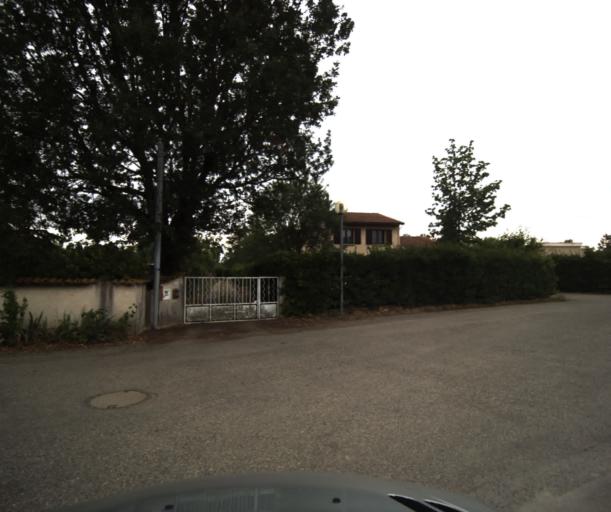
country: FR
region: Midi-Pyrenees
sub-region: Departement de la Haute-Garonne
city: Pinsaguel
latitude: 43.5347
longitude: 1.3804
